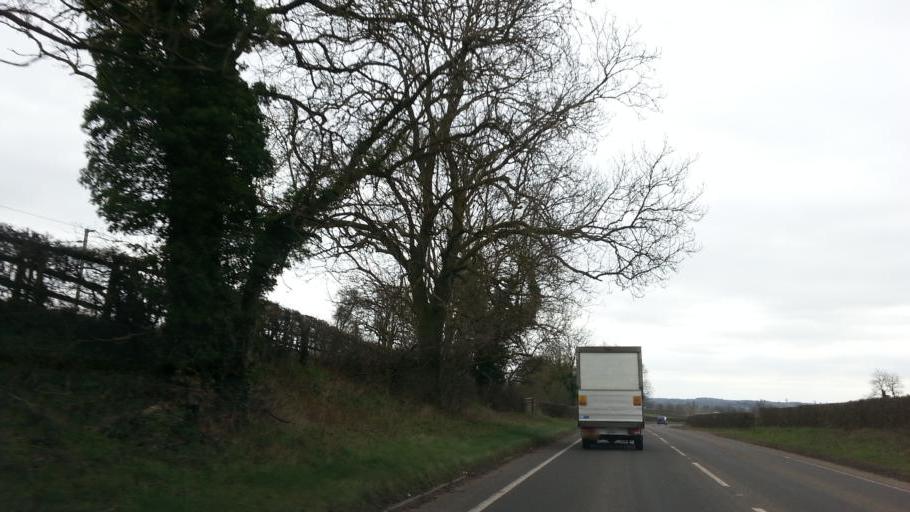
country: GB
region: England
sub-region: Staffordshire
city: Stone
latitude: 52.8839
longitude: -2.1177
